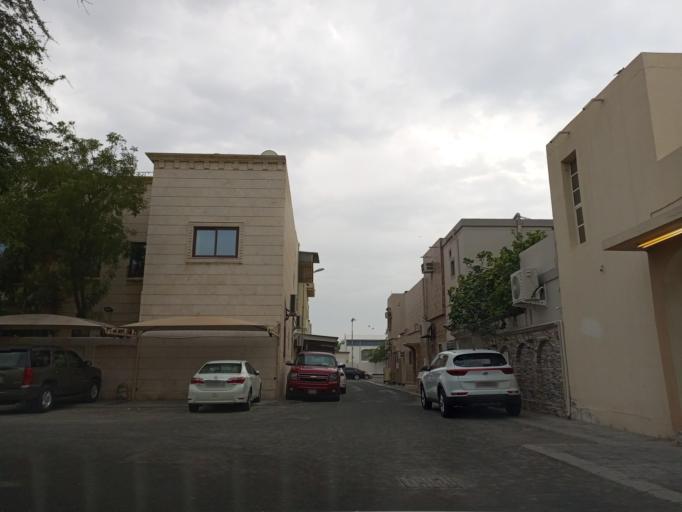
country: BH
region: Muharraq
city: Al Muharraq
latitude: 26.2584
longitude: 50.6330
